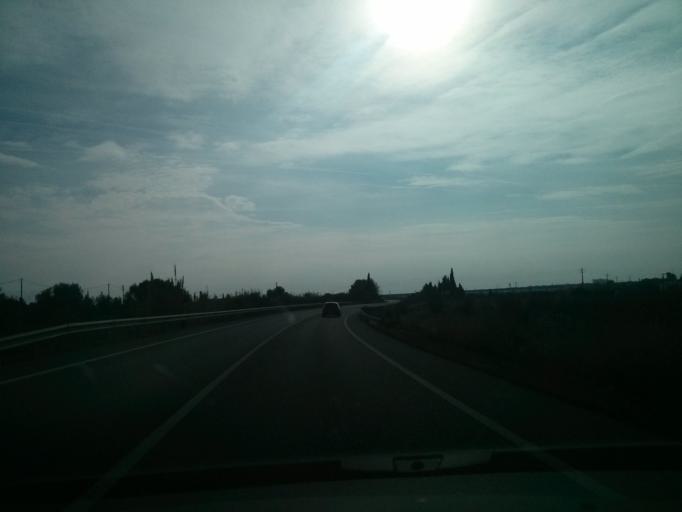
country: ES
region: Catalonia
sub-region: Provincia de Tarragona
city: El Vendrell
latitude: 41.2040
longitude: 1.5343
